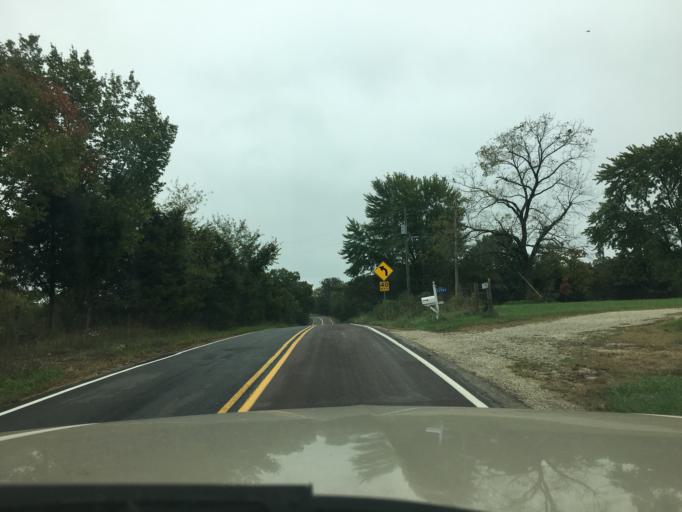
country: US
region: Missouri
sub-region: Crawford County
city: Cuba
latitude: 38.1912
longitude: -91.4744
